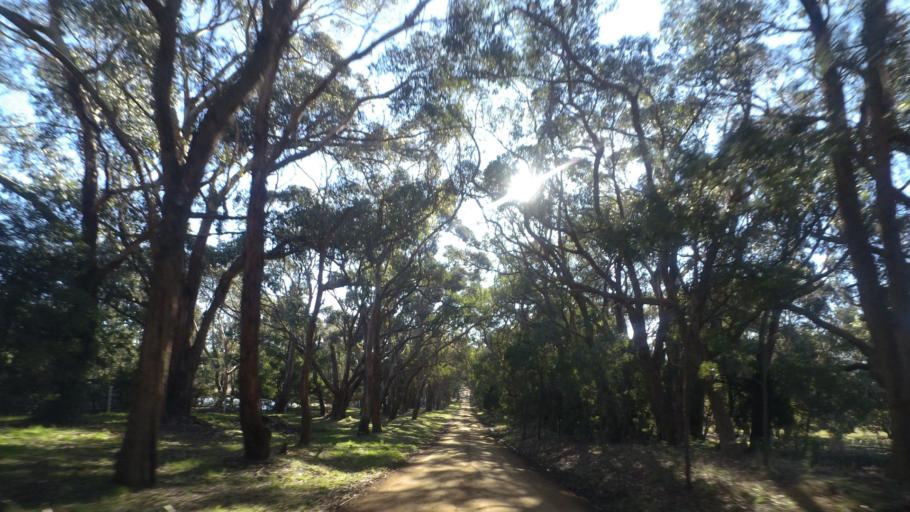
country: AU
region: Victoria
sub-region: Mount Alexander
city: Castlemaine
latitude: -37.2966
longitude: 144.3329
